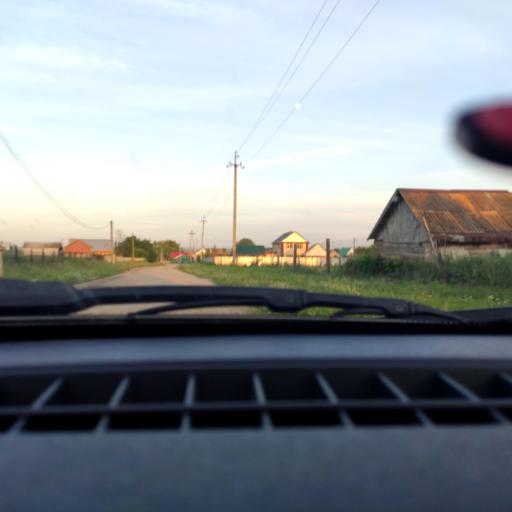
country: RU
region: Bashkortostan
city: Tolbazy
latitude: 54.2967
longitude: 55.8139
